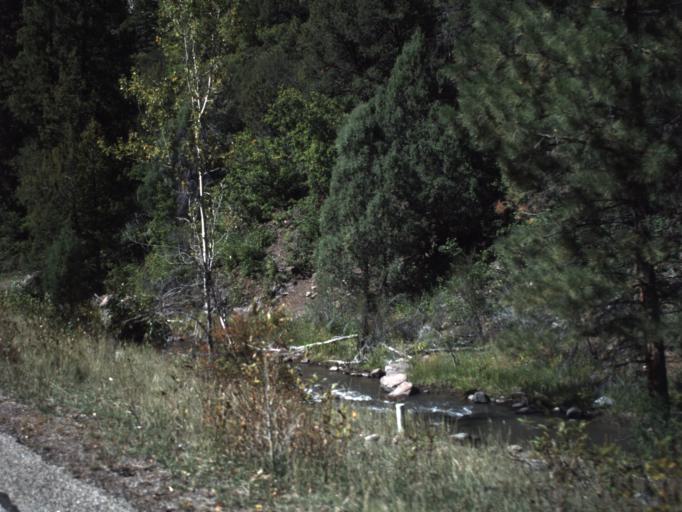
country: US
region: Utah
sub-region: Beaver County
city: Beaver
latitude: 38.2615
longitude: -112.5165
